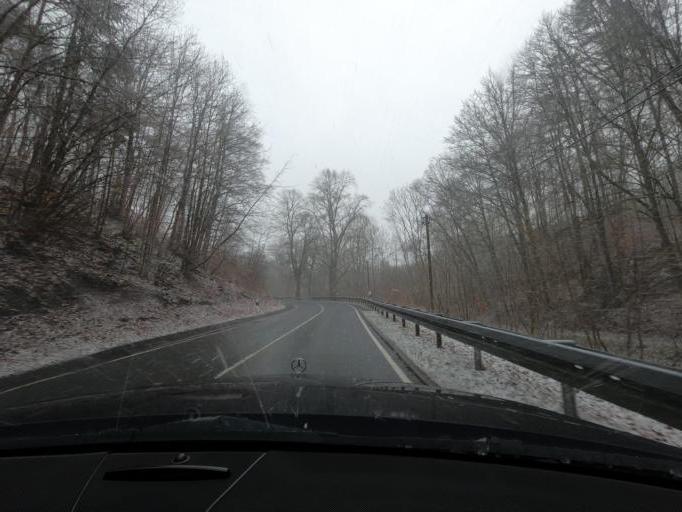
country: DE
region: Thuringia
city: Effelder
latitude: 51.2461
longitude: 10.2454
